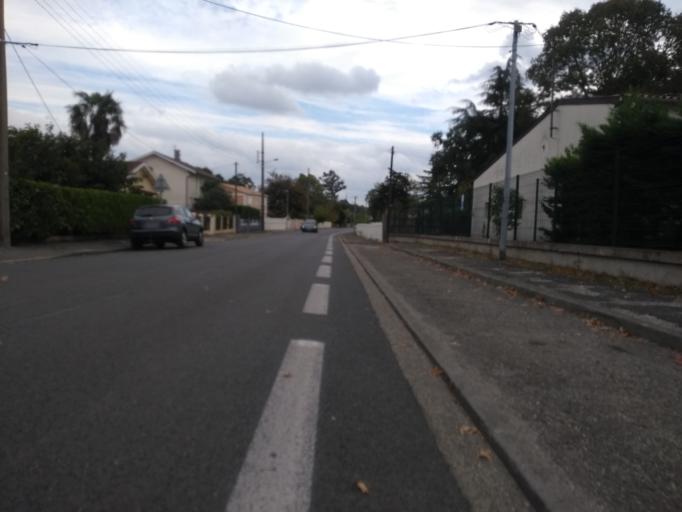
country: FR
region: Aquitaine
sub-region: Departement de la Gironde
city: Pessac
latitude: 44.8248
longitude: -0.6626
